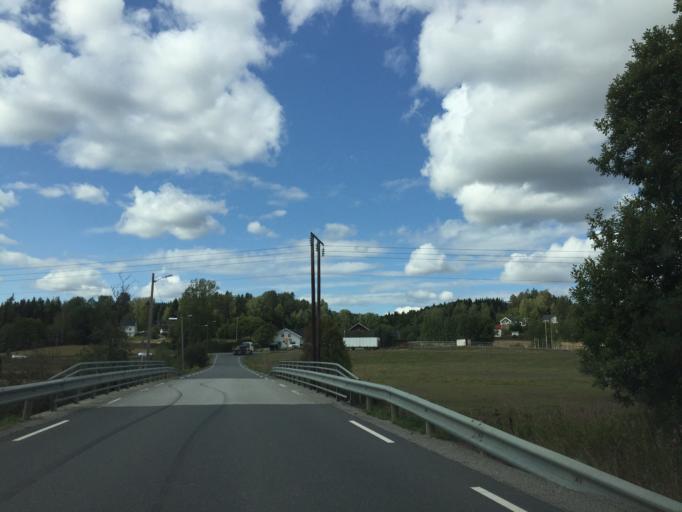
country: NO
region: Ostfold
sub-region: Hobol
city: Elvestad
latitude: 59.6066
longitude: 10.9195
